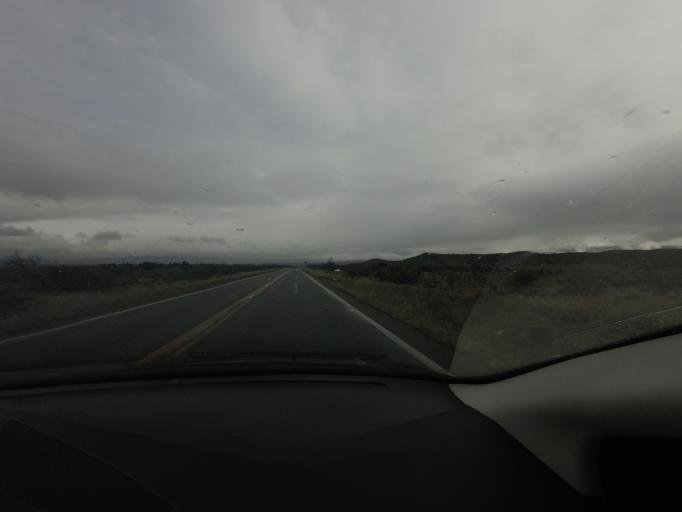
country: US
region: Arizona
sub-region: Yavapai County
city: Lake Montezuma
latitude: 34.6756
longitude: -111.8379
